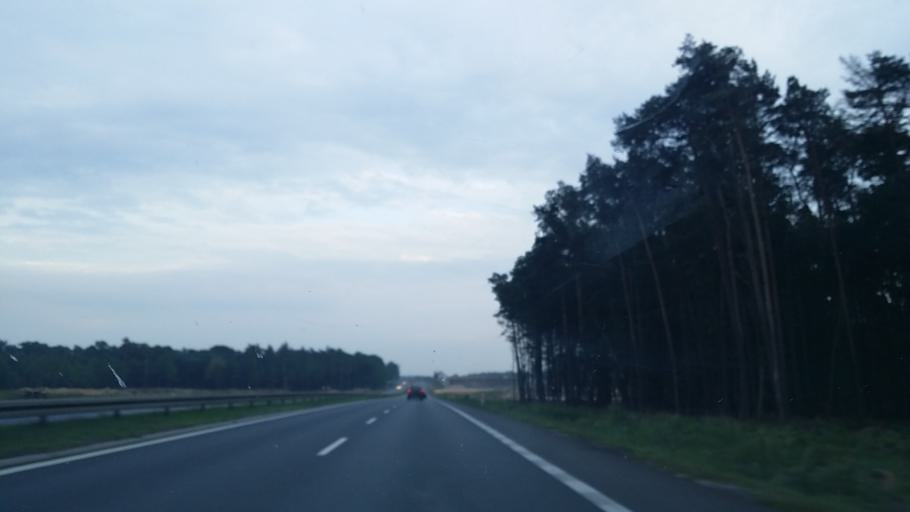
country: PL
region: Lower Silesian Voivodeship
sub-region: Powiat polkowicki
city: Polkowice
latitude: 51.4804
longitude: 16.0908
